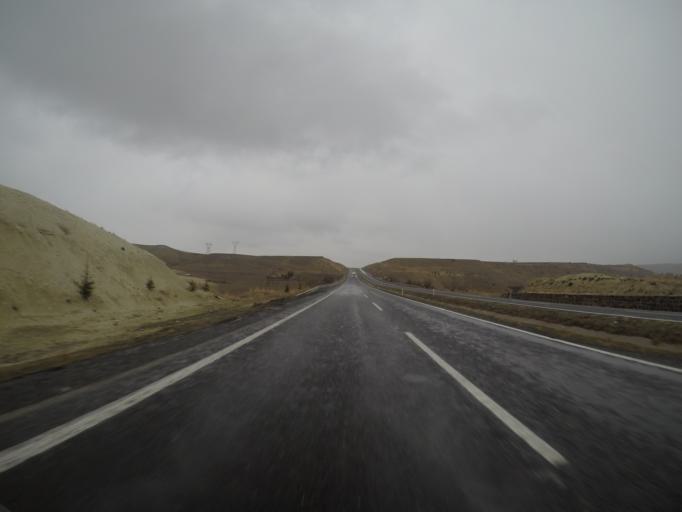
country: TR
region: Nevsehir
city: Urgub
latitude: 38.7422
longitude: 35.0081
